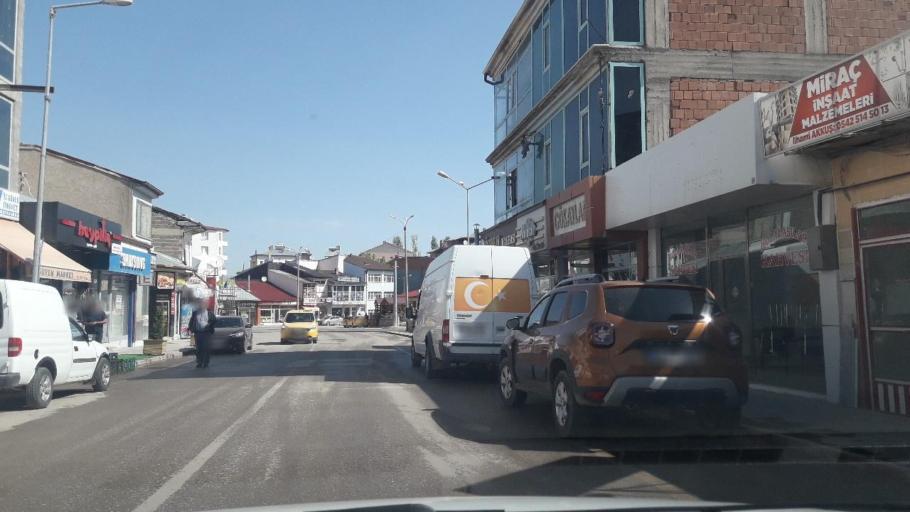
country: TR
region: Sivas
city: Kangal
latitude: 39.2349
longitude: 37.3911
